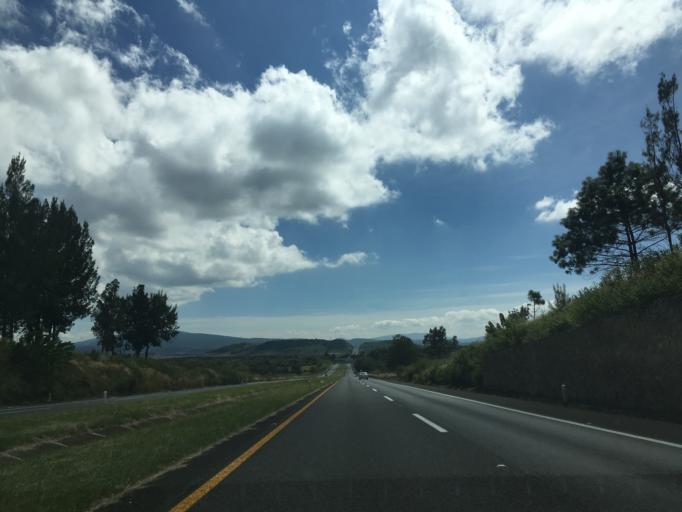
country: MX
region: Michoacan
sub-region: Puruandiro
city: San Lorenzo
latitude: 19.9558
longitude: -101.6597
